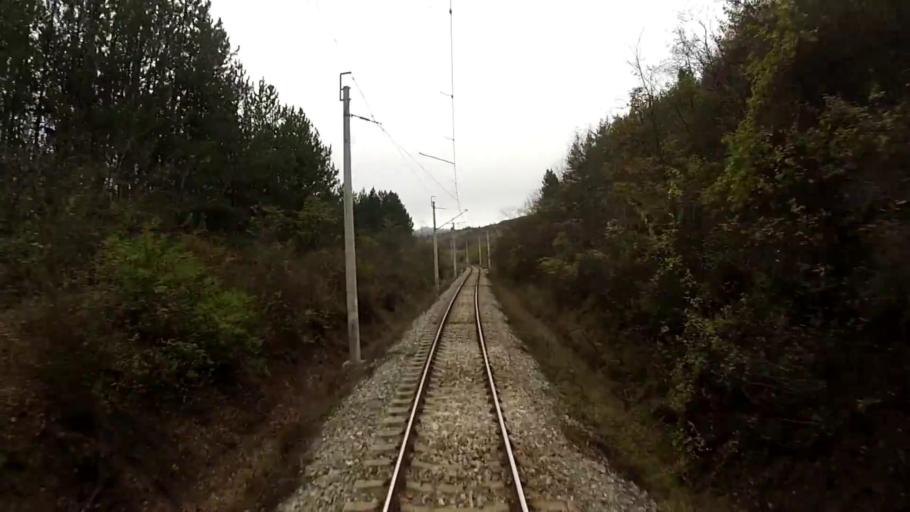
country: BG
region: Sofiya
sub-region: Obshtina Dragoman
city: Dragoman
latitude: 42.9429
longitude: 22.9015
